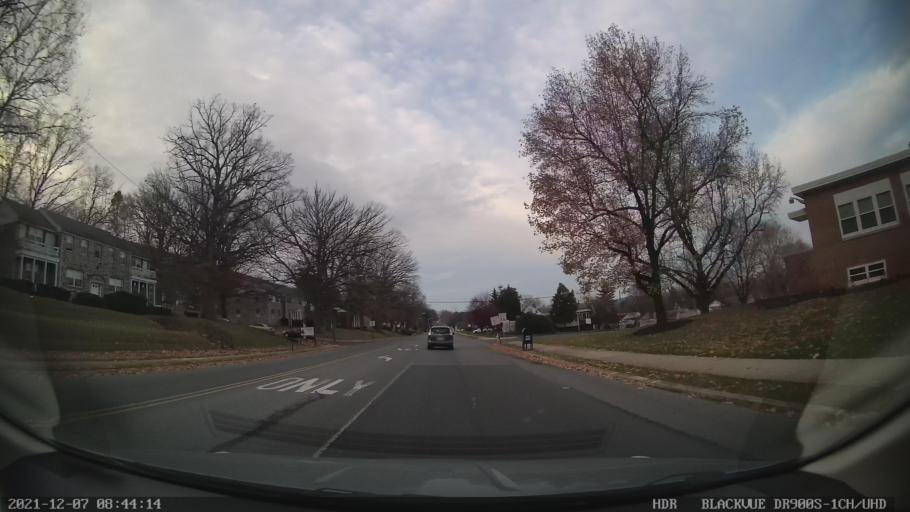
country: US
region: Pennsylvania
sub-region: Berks County
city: Hyde Park
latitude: 40.3656
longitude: -75.9021
